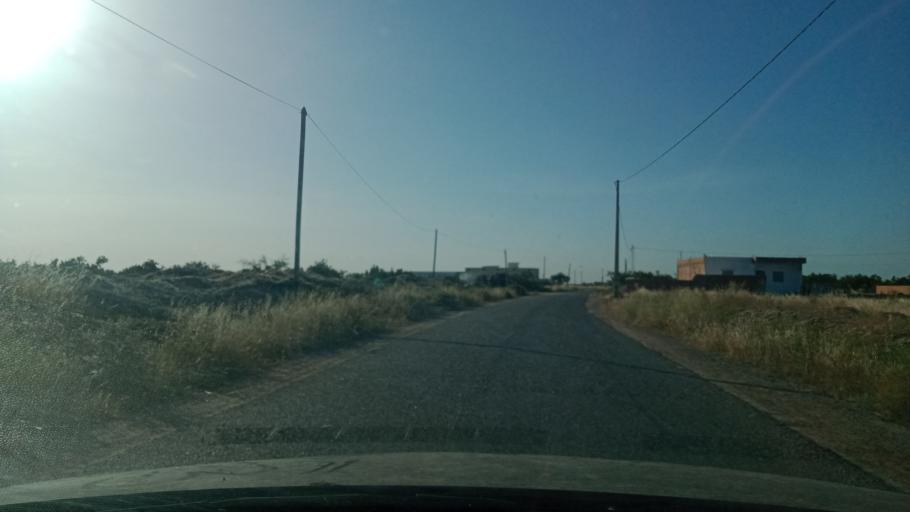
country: TN
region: Safaqis
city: Sfax
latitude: 34.8258
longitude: 10.7363
